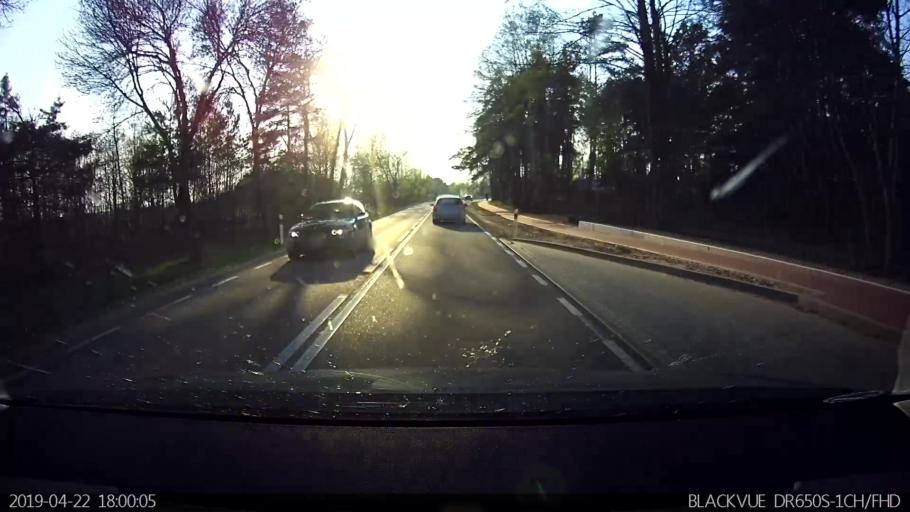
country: PL
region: Masovian Voivodeship
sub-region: Powiat wegrowski
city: Korytnica
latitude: 52.4752
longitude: 21.8514
